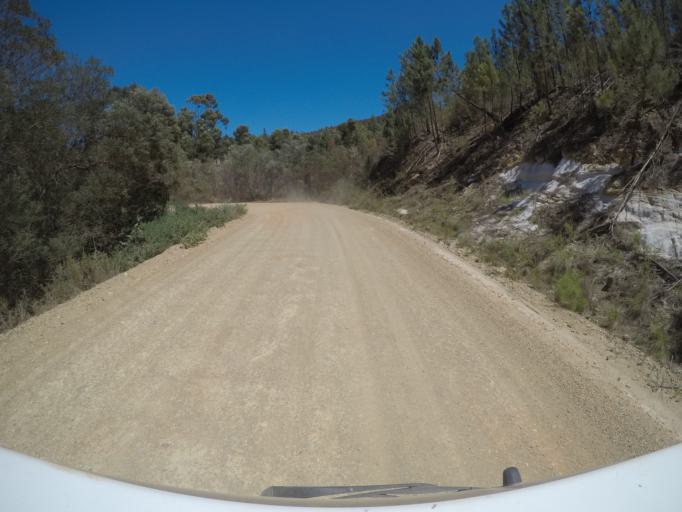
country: ZA
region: Western Cape
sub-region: Overberg District Municipality
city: Grabouw
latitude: -34.1584
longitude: 19.2262
